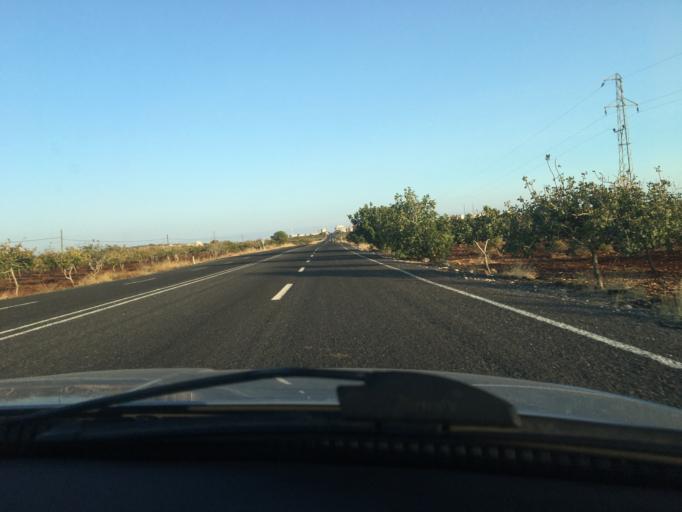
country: TR
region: Sanliurfa
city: Halfeti
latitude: 37.2385
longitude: 37.9189
